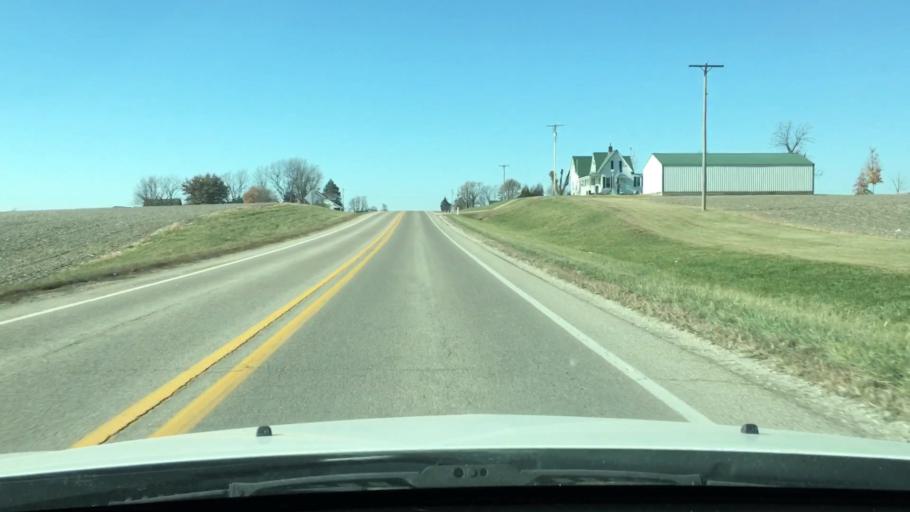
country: US
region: Illinois
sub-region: Pike County
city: Pittsfield
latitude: 39.6048
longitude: -90.8507
